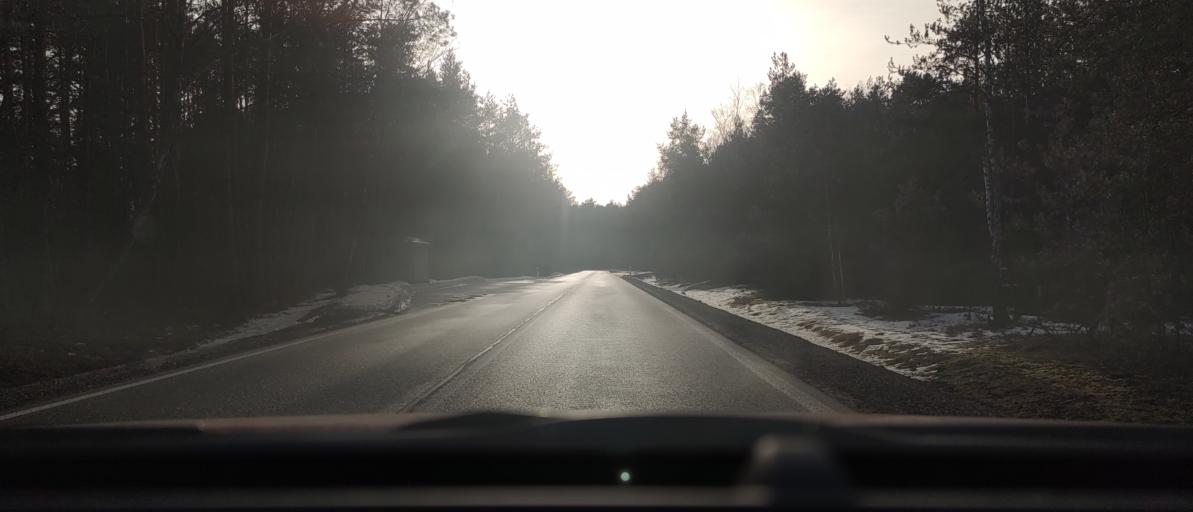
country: PL
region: Masovian Voivodeship
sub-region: Powiat bialobrzeski
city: Sucha
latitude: 51.6304
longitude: 20.8888
